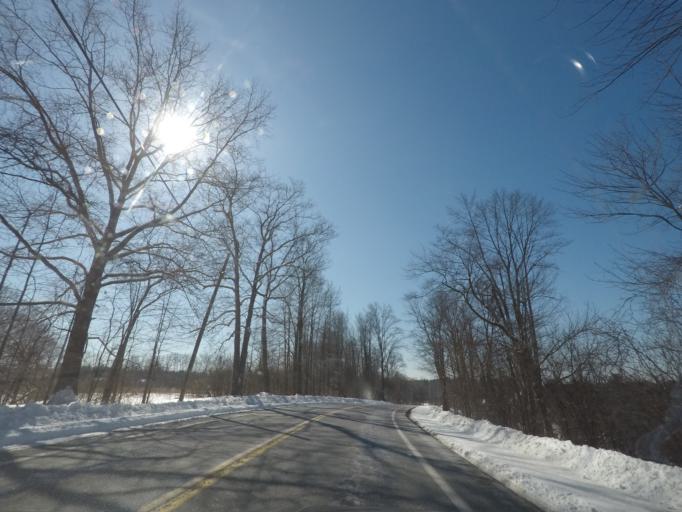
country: US
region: New York
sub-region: Saratoga County
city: Ballston Spa
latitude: 42.9942
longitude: -73.8266
